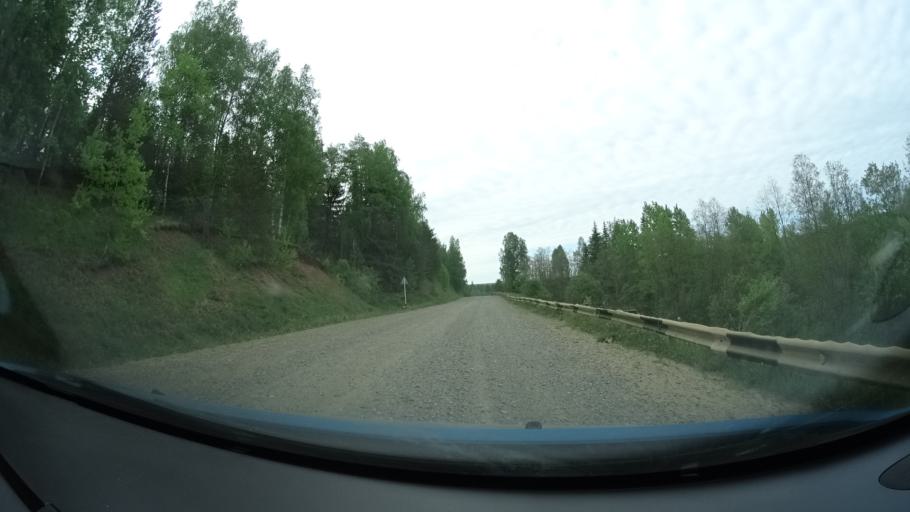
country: RU
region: Perm
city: Kuyeda
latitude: 56.6534
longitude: 55.6939
